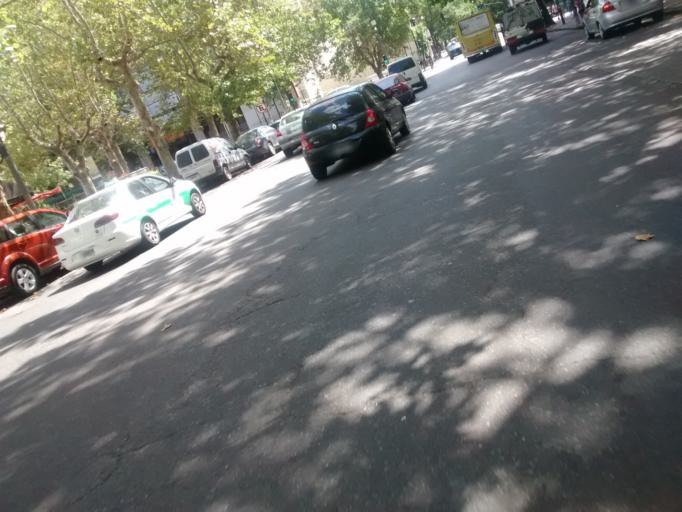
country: AR
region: Buenos Aires
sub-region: Partido de La Plata
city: La Plata
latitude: -34.9227
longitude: -57.9536
